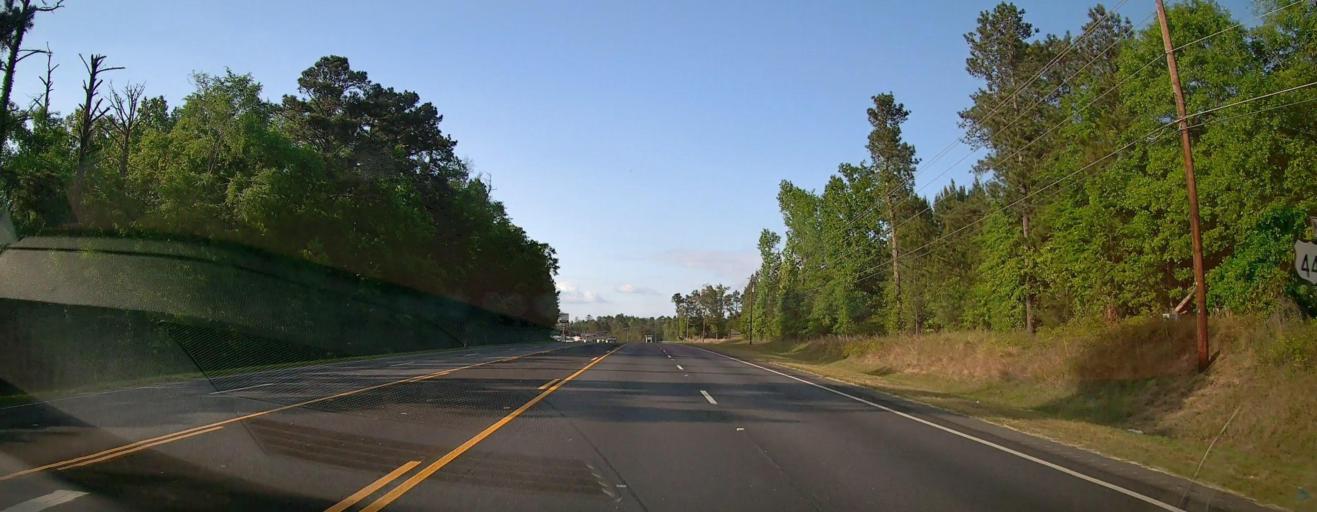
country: US
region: Georgia
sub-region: Baldwin County
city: Milledgeville
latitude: 33.1372
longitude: -83.2708
